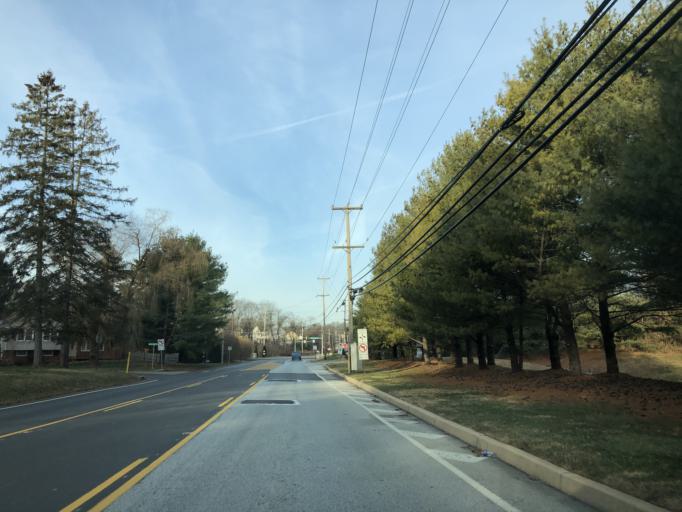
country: US
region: Pennsylvania
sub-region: Chester County
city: Exton
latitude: 40.0083
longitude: -75.5891
